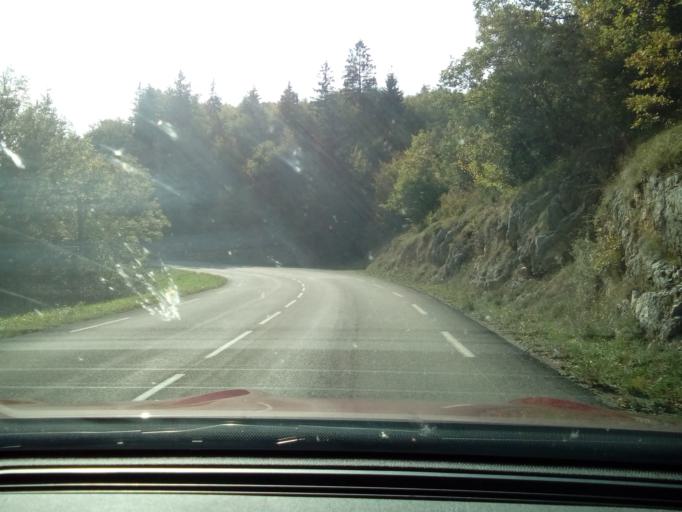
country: FR
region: Rhone-Alpes
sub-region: Departement de la Drome
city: Saint-Laurent-en-Royans
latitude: 44.9921
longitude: 5.4132
